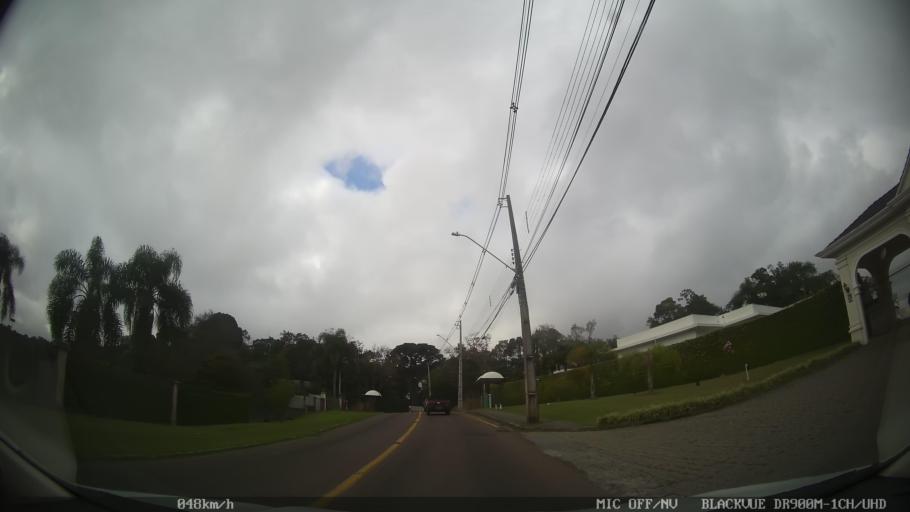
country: BR
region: Parana
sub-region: Curitiba
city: Curitiba
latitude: -25.3624
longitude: -49.2439
